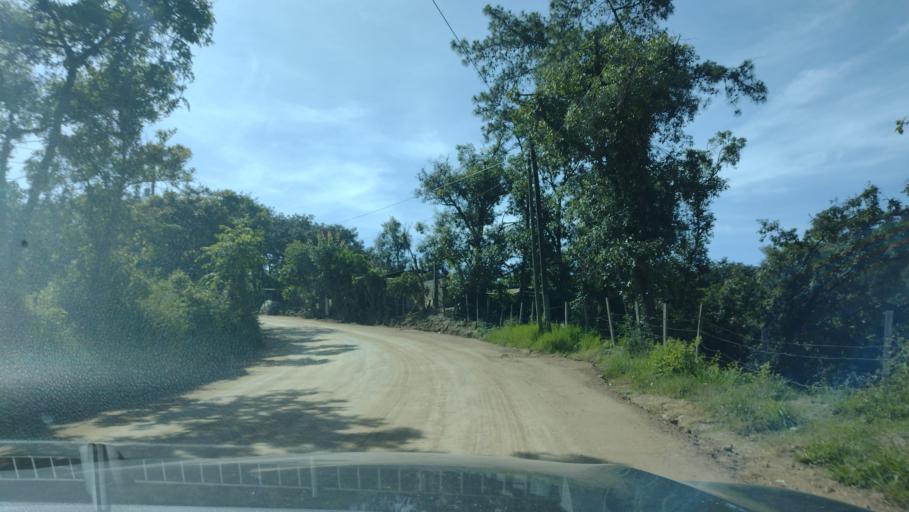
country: GT
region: Guatemala
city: Chinautla
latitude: 14.7602
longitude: -90.5223
